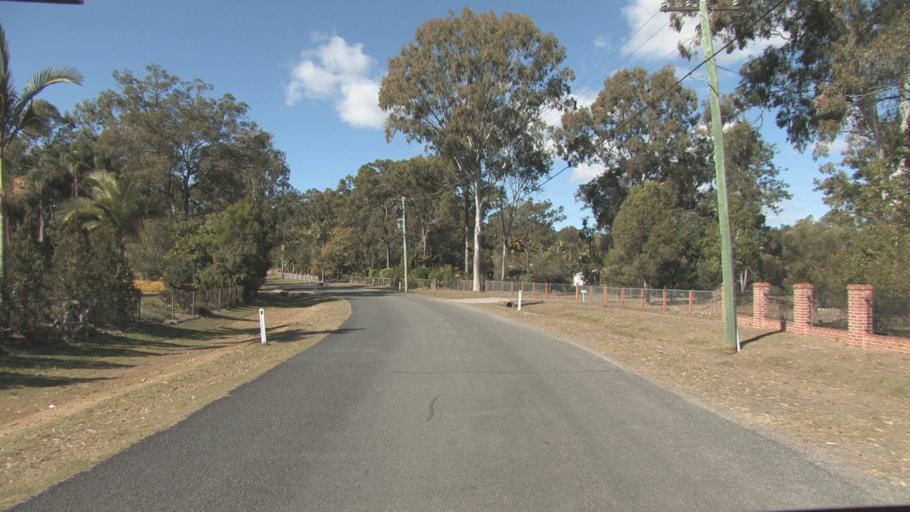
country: AU
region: Queensland
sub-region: Logan
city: Chambers Flat
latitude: -27.7465
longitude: 153.0952
